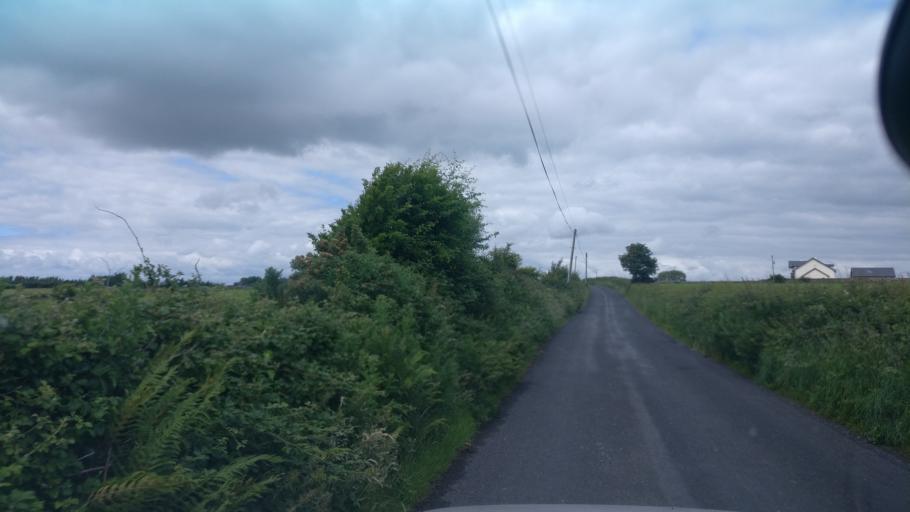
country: IE
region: Connaught
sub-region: County Galway
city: Loughrea
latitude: 53.1661
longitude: -8.5532
